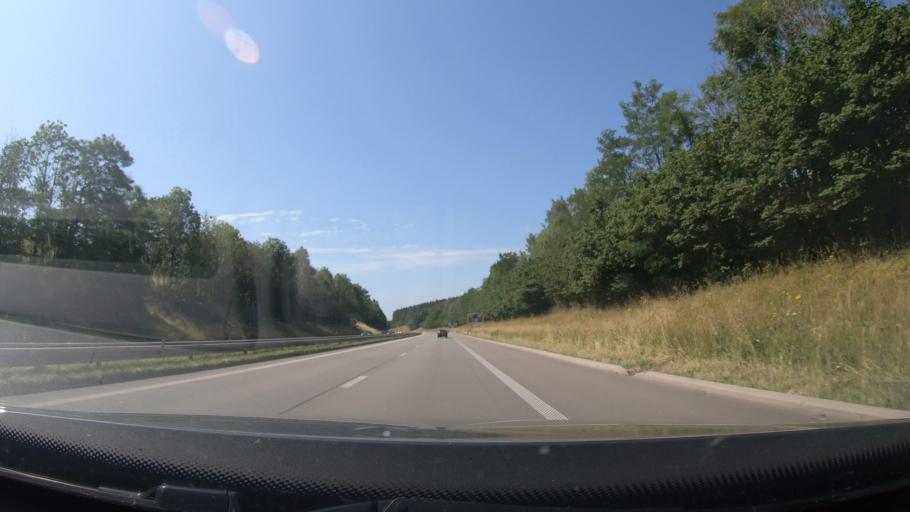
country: BE
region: Wallonia
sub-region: Province de Liege
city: Saint-Vith
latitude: 50.3091
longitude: 6.0805
